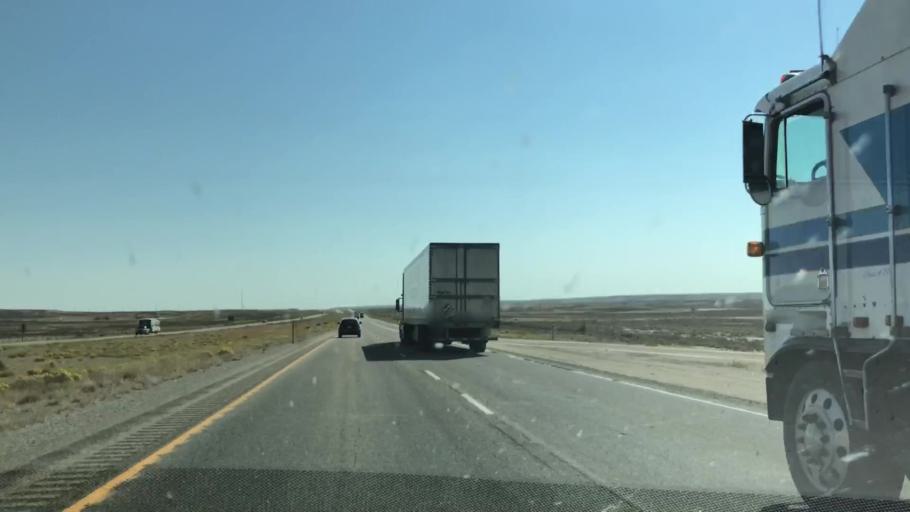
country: US
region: Wyoming
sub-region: Sweetwater County
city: Rock Springs
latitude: 41.6330
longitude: -108.3769
